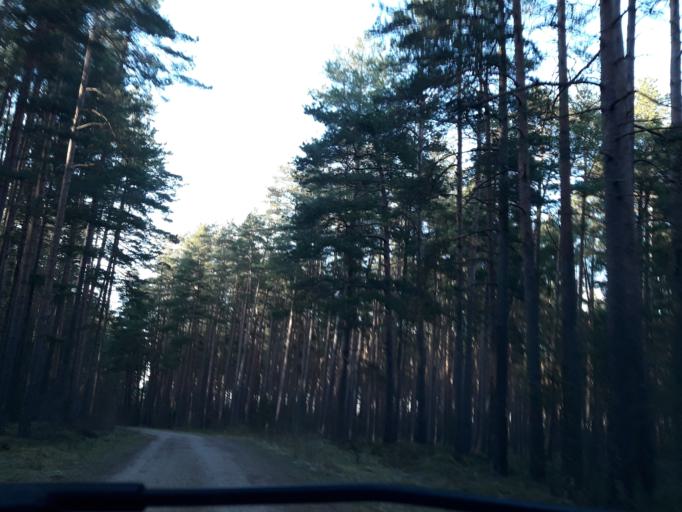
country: LV
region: Kekava
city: Kekava
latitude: 56.8666
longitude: 24.2214
